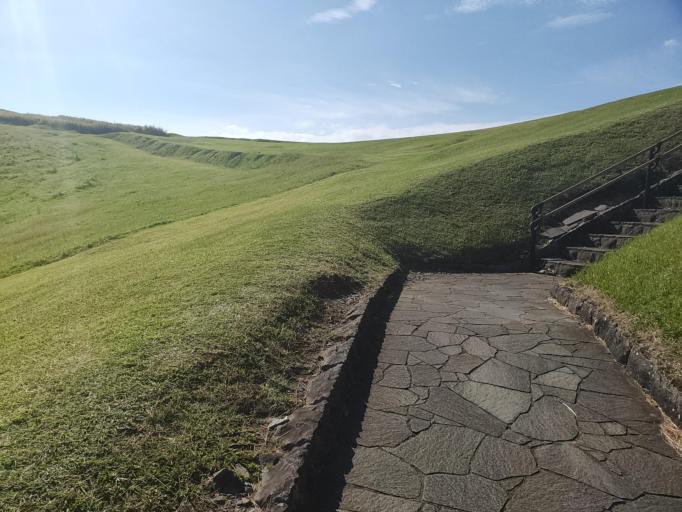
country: JP
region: Nagasaki
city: Fukuecho
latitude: 32.6628
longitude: 128.8507
